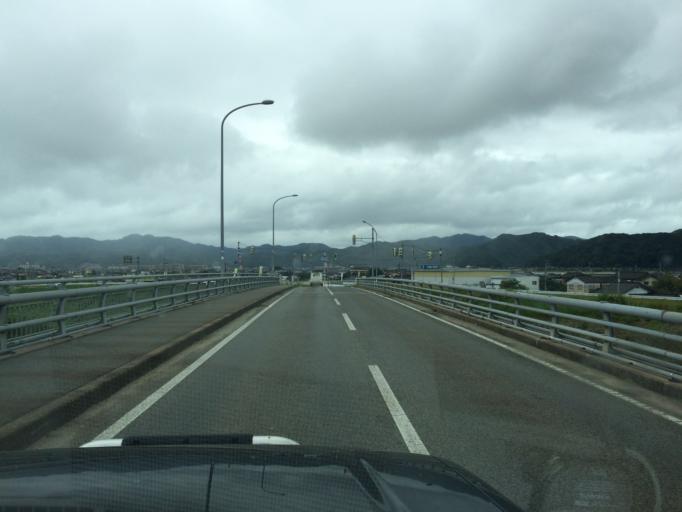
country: JP
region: Hyogo
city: Toyooka
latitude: 35.5127
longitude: 134.8261
